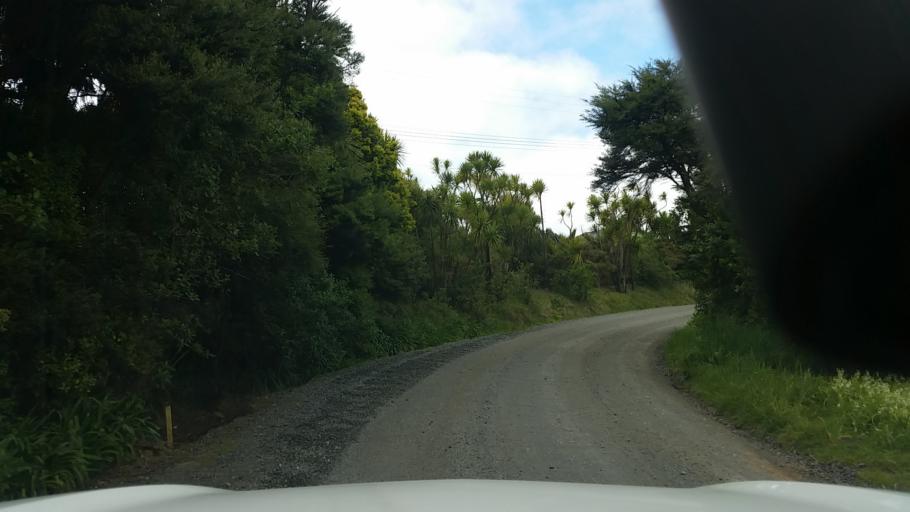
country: NZ
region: Auckland
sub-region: Auckland
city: Muriwai Beach
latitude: -36.8515
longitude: 174.4840
